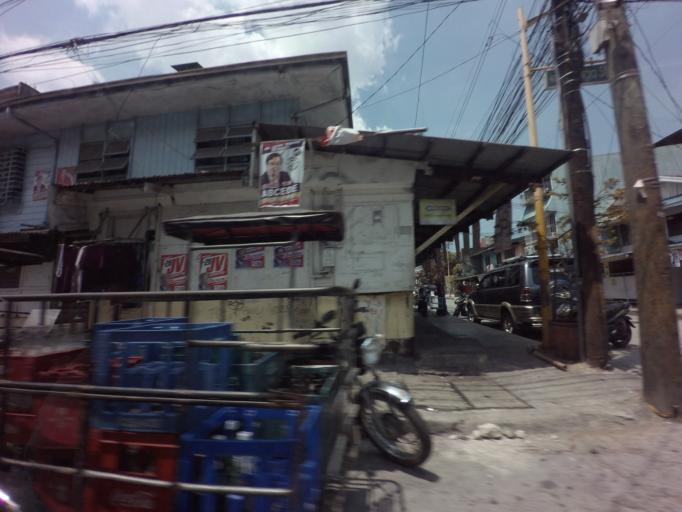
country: PH
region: Metro Manila
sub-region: Mandaluyong
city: Mandaluyong City
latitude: 14.5729
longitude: 121.0228
